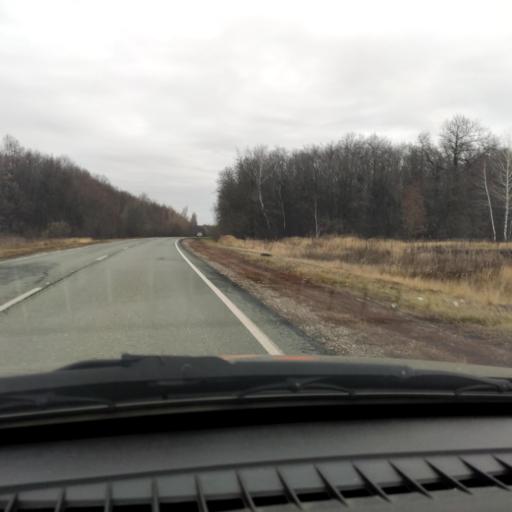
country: RU
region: Samara
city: Zhigulevsk
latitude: 53.3411
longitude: 49.4512
